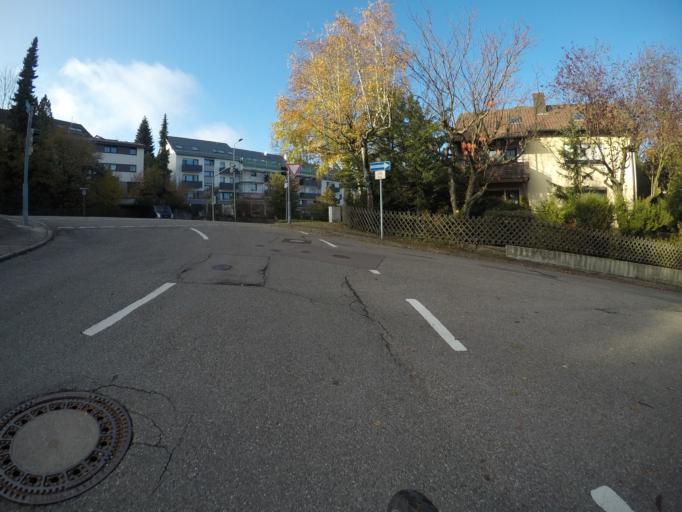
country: DE
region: Baden-Wuerttemberg
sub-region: Regierungsbezirk Stuttgart
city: Steinenbronn
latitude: 48.7149
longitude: 9.1056
